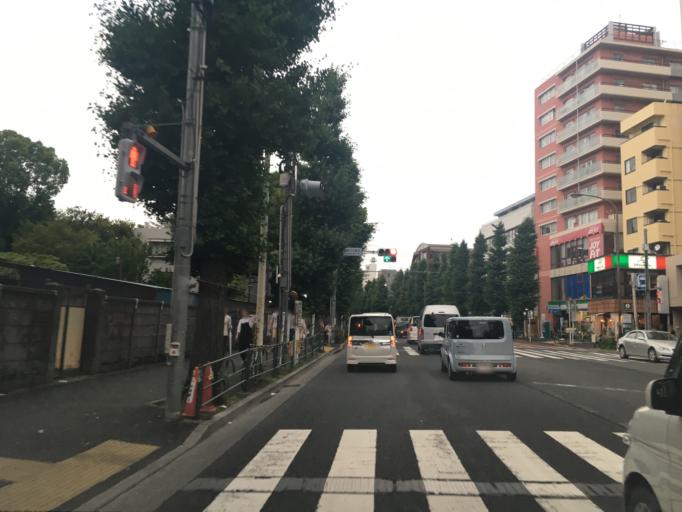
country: JP
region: Tokyo
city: Tokyo
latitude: 35.6979
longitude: 139.6584
